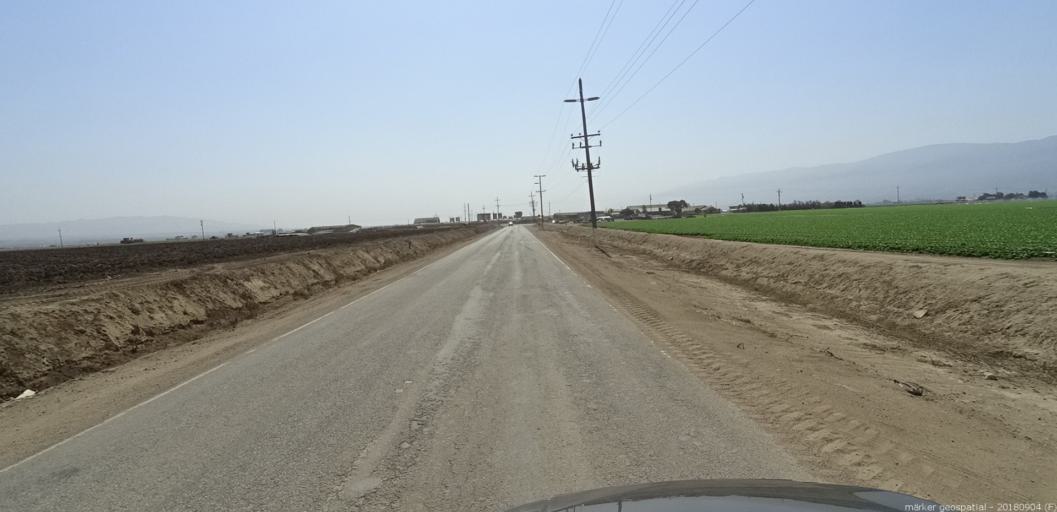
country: US
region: California
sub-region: Monterey County
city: Gonzales
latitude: 36.5393
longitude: -121.4644
